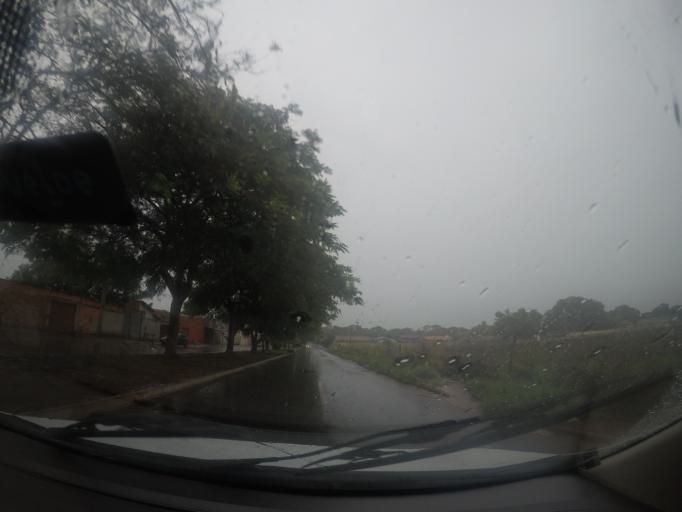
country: BR
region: Goias
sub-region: Goiania
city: Goiania
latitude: -16.5964
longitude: -49.3256
